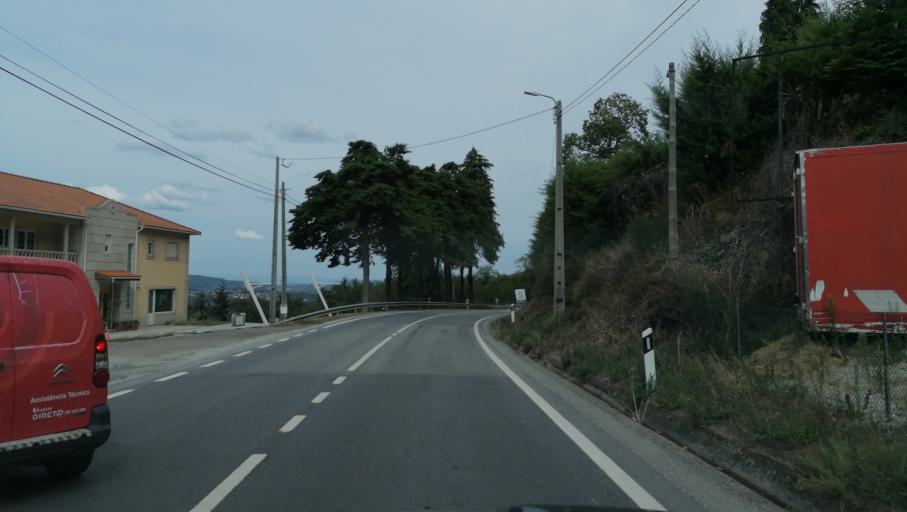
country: PT
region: Vila Real
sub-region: Vila Pouca de Aguiar
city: Vila Pouca de Aguiar
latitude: 41.5086
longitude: -7.6308
